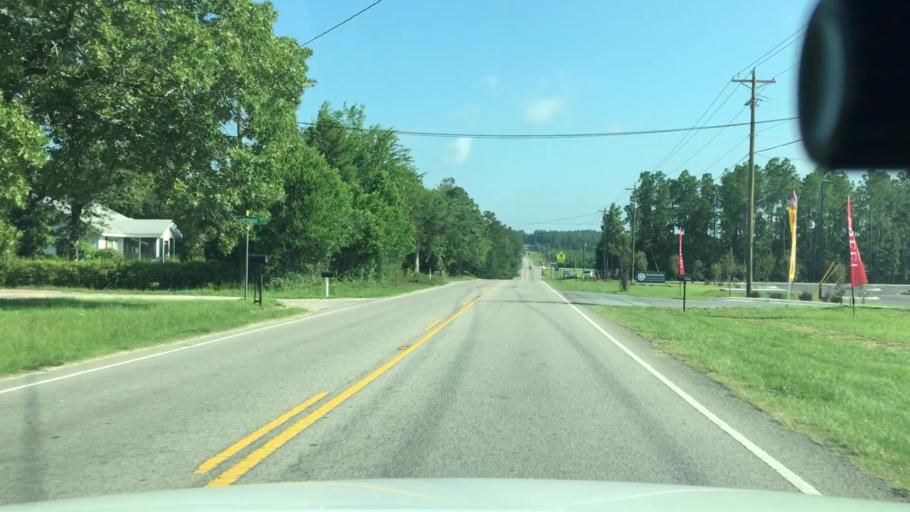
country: US
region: South Carolina
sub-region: Aiken County
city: Graniteville
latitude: 33.5791
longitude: -81.8359
